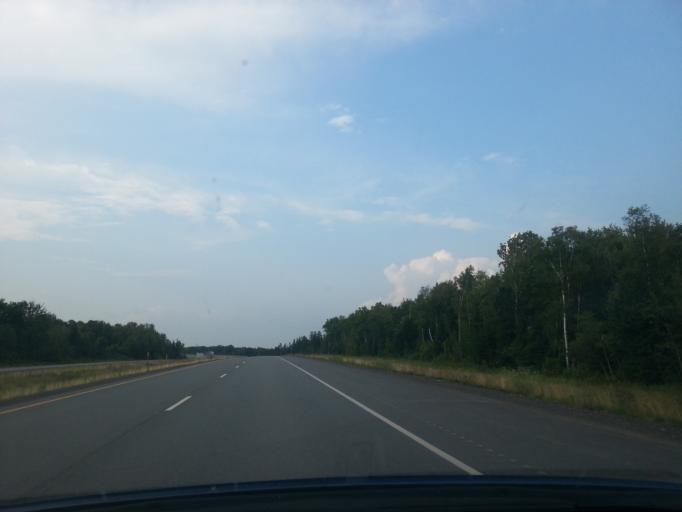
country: CA
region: New Brunswick
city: Harrison Brook
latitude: 47.2027
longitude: -67.9308
